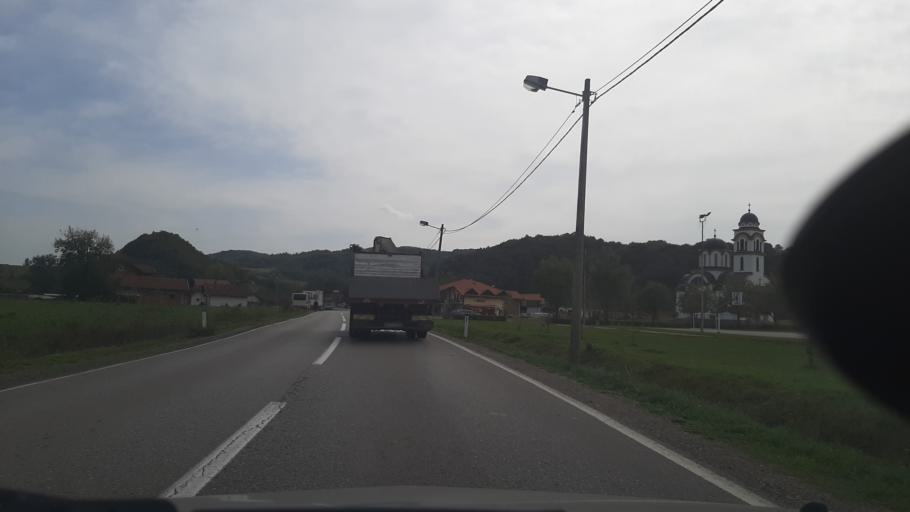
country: BA
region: Republika Srpska
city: Maglajani
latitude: 44.8578
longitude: 17.4395
